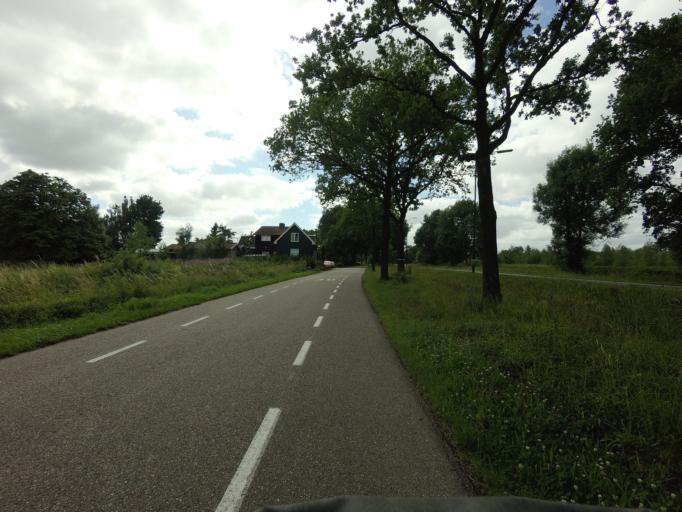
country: NL
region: Utrecht
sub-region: Gemeente Utrecht
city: Lunetten
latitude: 52.0643
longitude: 5.1636
